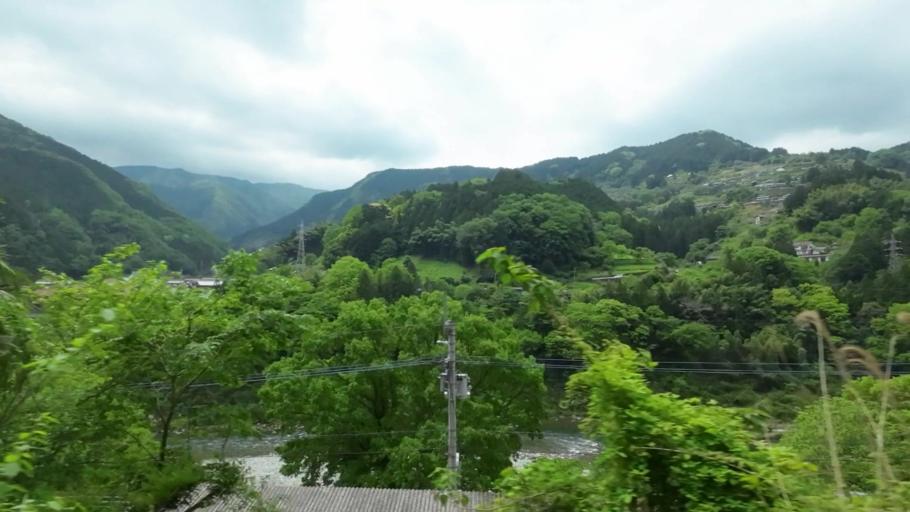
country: JP
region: Tokushima
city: Ikedacho
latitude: 33.9706
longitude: 133.7728
